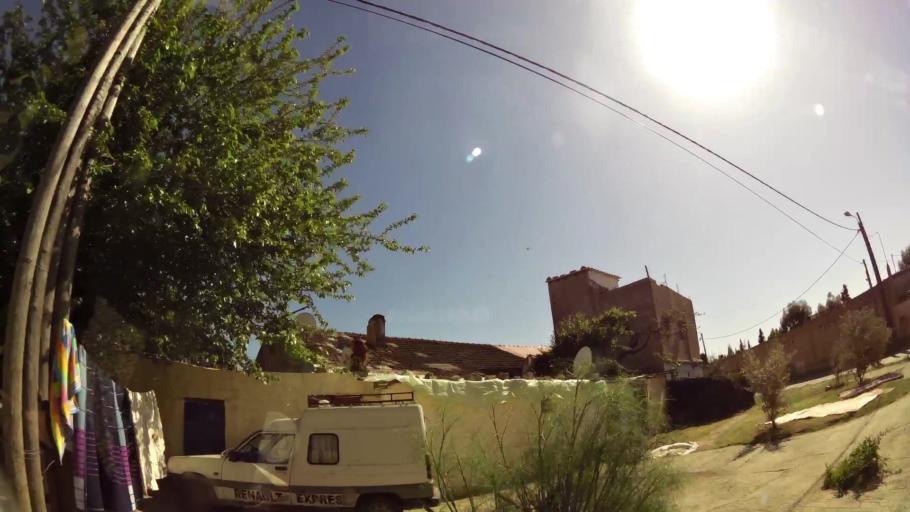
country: MA
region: Meknes-Tafilalet
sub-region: Meknes
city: Meknes
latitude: 33.8911
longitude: -5.5294
